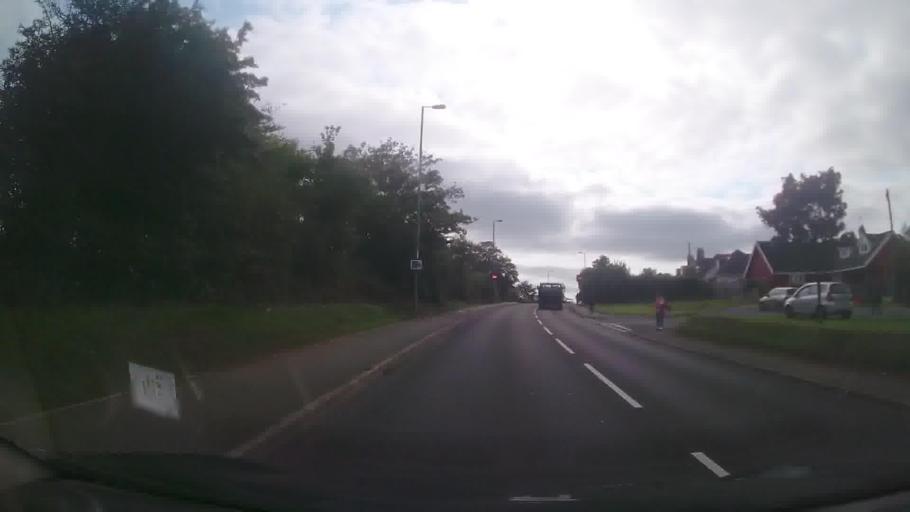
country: GB
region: Wales
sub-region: Pembrokeshire
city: Steynton
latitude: 51.7249
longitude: -5.0198
